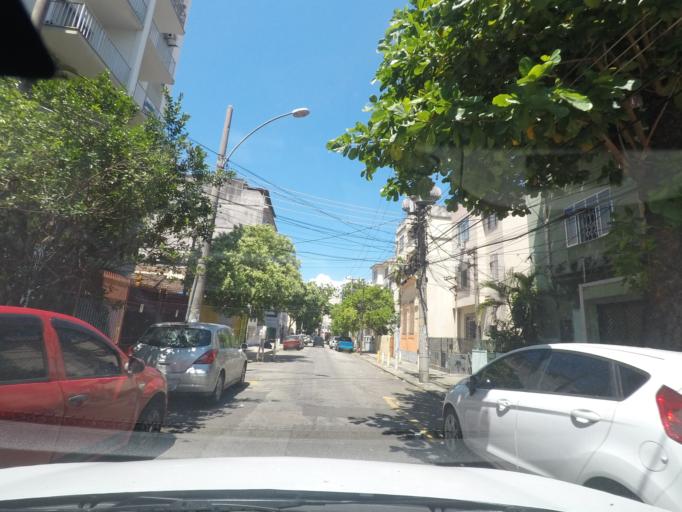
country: BR
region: Rio de Janeiro
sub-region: Rio De Janeiro
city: Rio de Janeiro
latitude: -22.9181
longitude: -43.2377
